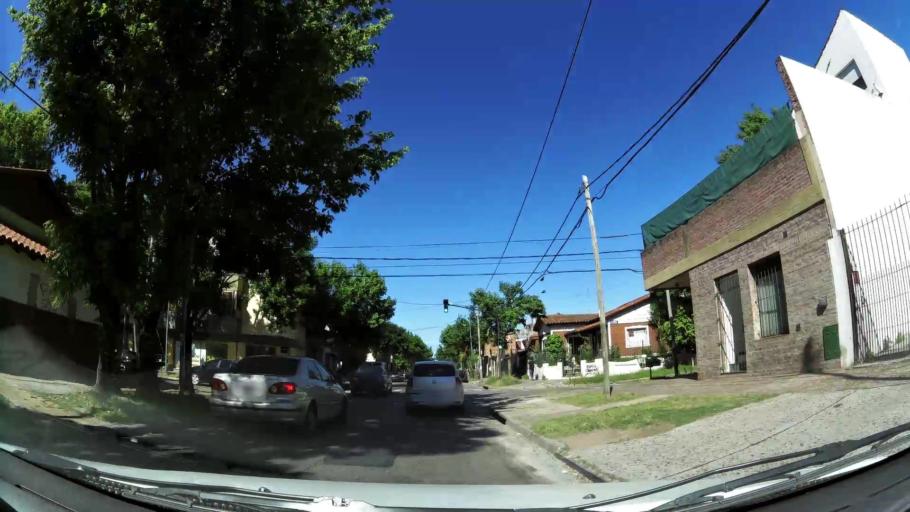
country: AR
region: Buenos Aires
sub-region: Partido de General San Martin
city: General San Martin
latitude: -34.5399
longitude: -58.5096
